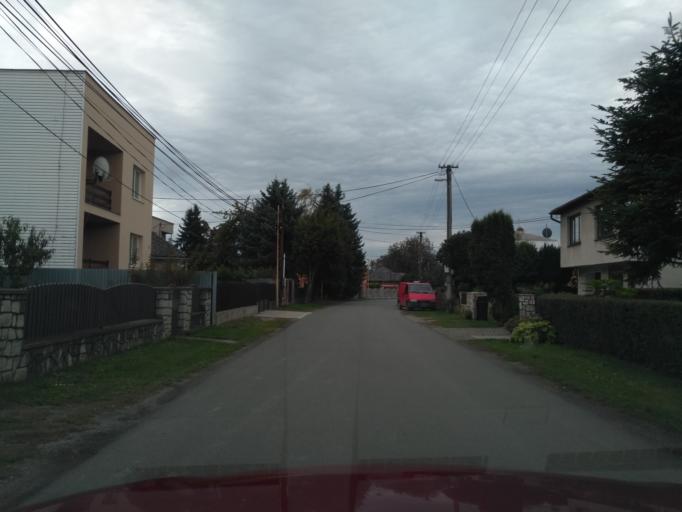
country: SK
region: Kosicky
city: Kosice
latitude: 48.6747
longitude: 21.3110
